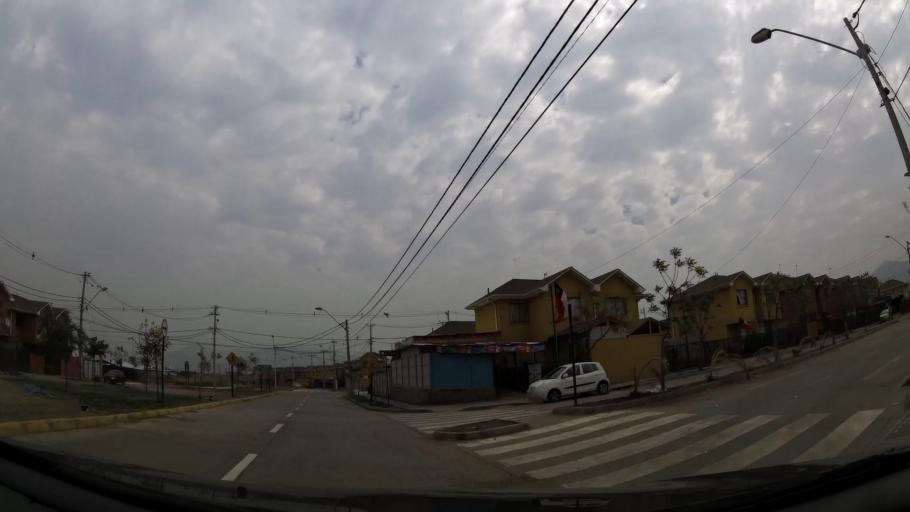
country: CL
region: Santiago Metropolitan
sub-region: Provincia de Chacabuco
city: Chicureo Abajo
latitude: -33.1927
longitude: -70.6787
